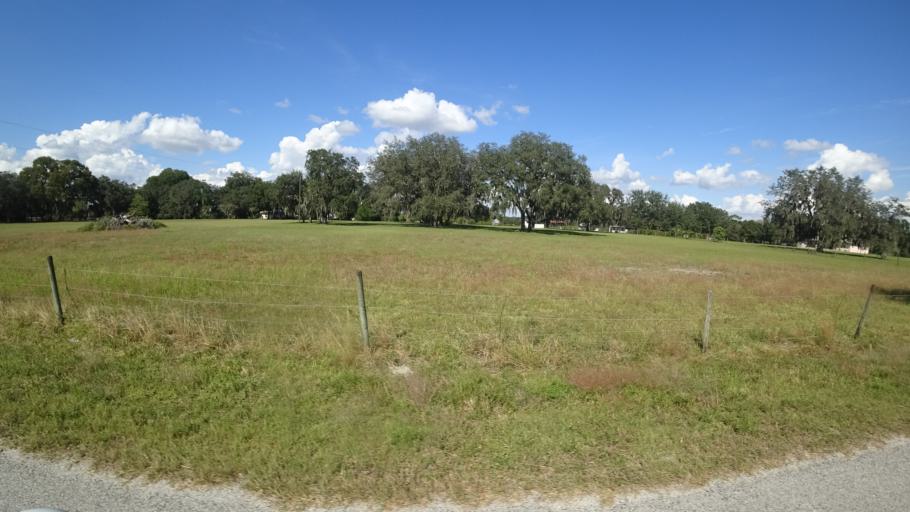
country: US
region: Florida
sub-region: Sarasota County
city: The Meadows
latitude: 27.4672
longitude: -82.2978
